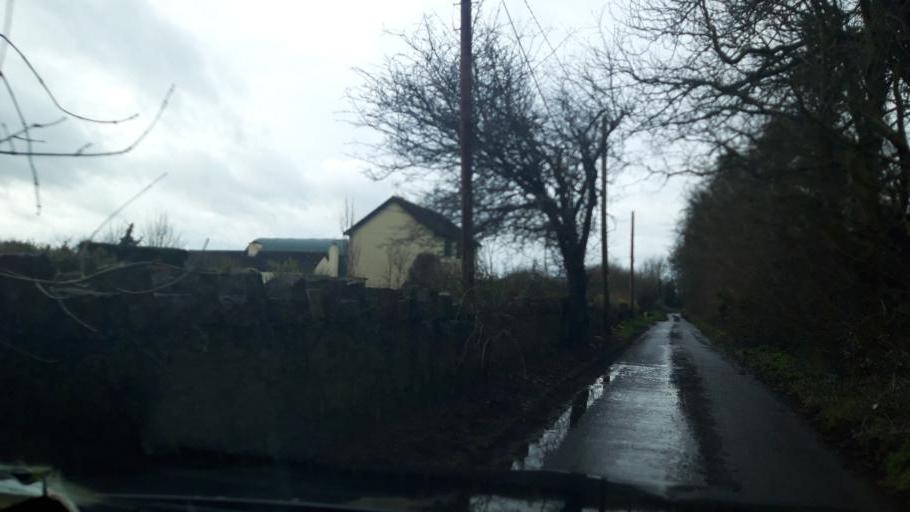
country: IE
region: Leinster
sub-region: South Dublin
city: Newcastle
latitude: 53.3233
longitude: -6.5119
